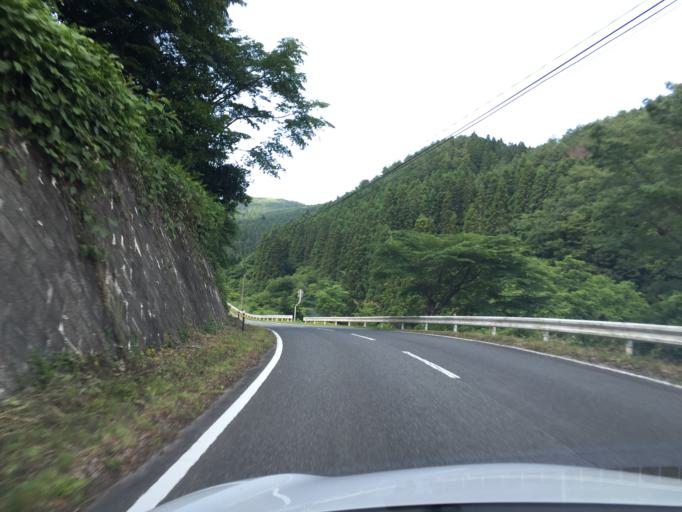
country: JP
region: Fukushima
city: Ishikawa
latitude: 37.1299
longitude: 140.6423
